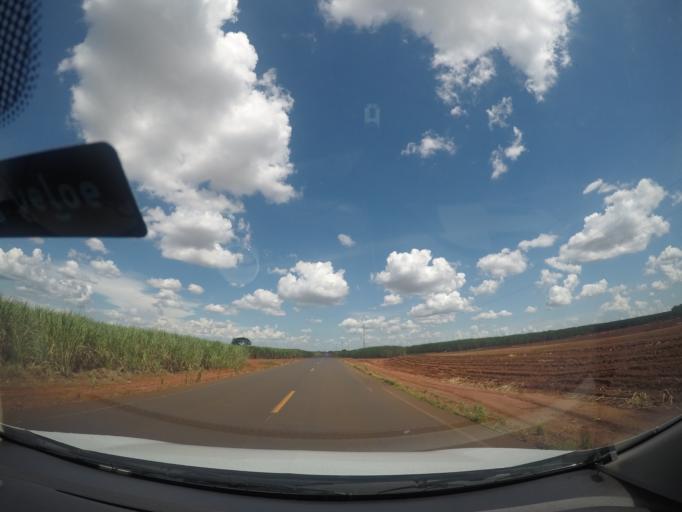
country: BR
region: Minas Gerais
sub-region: Frutal
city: Frutal
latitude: -19.8509
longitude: -48.7362
